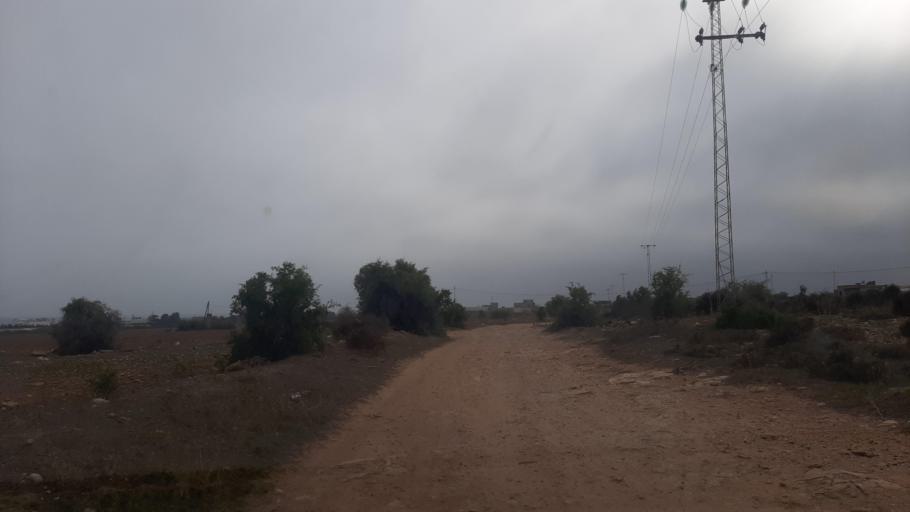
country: TN
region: Nabul
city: Menzel Heurr
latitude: 36.6890
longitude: 10.9325
